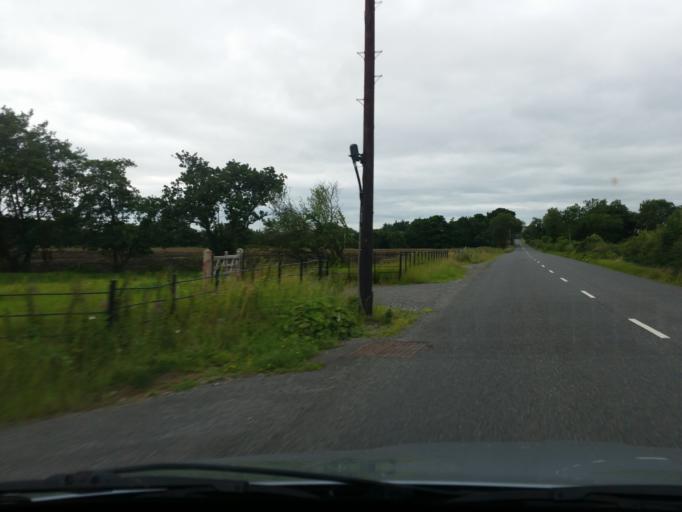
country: GB
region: Northern Ireland
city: Lisnaskea
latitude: 54.2341
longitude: -7.4541
